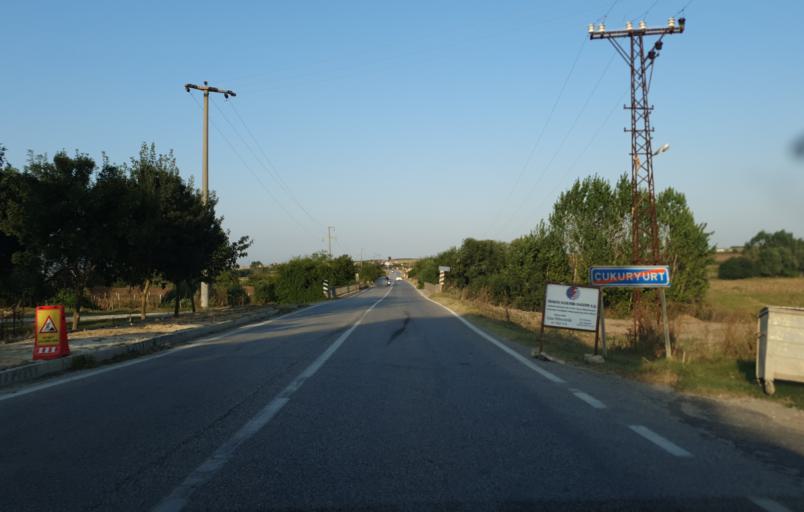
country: TR
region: Tekirdag
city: Saray
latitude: 41.4301
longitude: 27.8886
